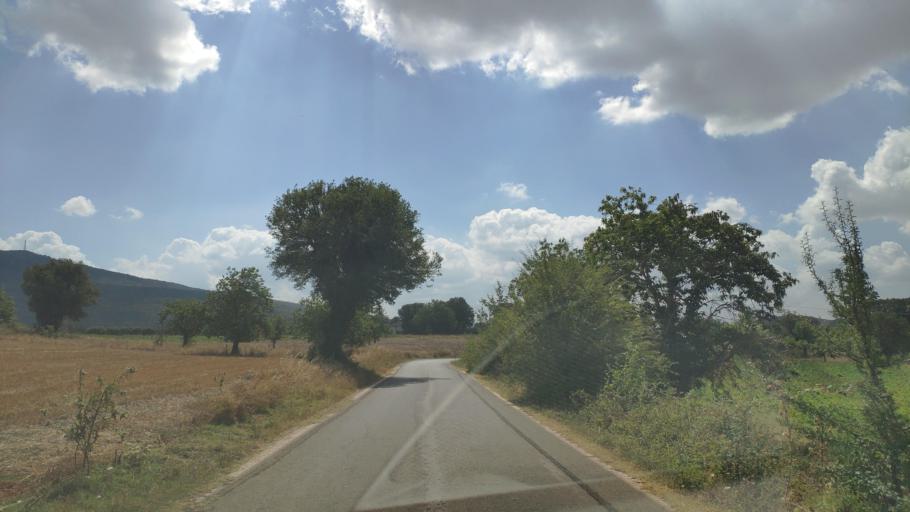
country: GR
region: Peloponnese
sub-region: Nomos Lakonias
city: Kariai
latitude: 37.3210
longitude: 22.4364
